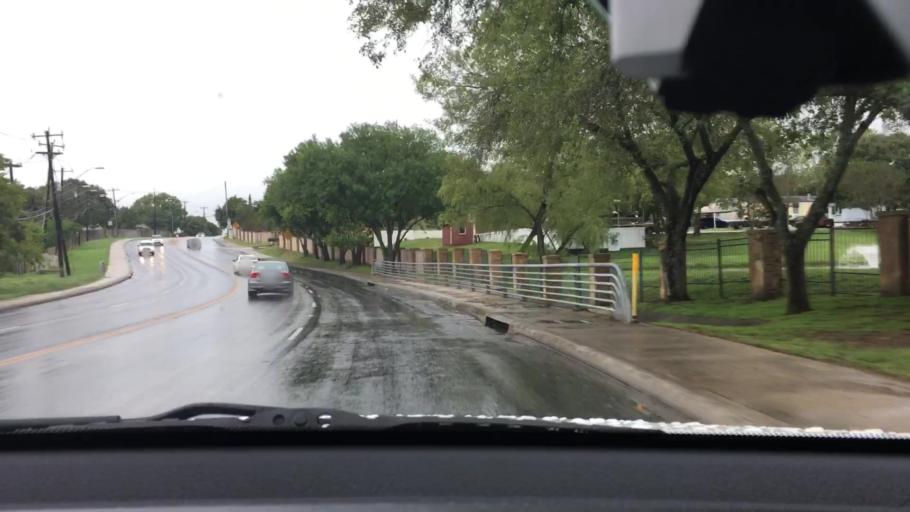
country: US
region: Texas
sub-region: Bexar County
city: Windcrest
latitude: 29.5216
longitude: -98.3621
